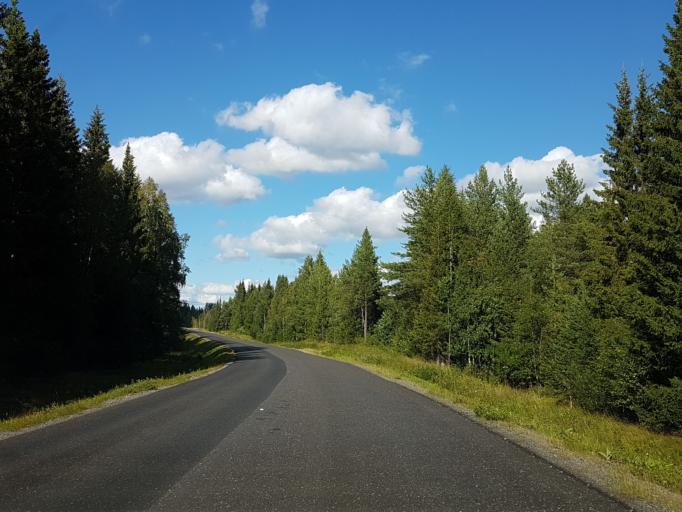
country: SE
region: Vaesterbotten
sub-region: Skelleftea Kommun
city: Burtraesk
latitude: 64.2962
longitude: 20.5268
